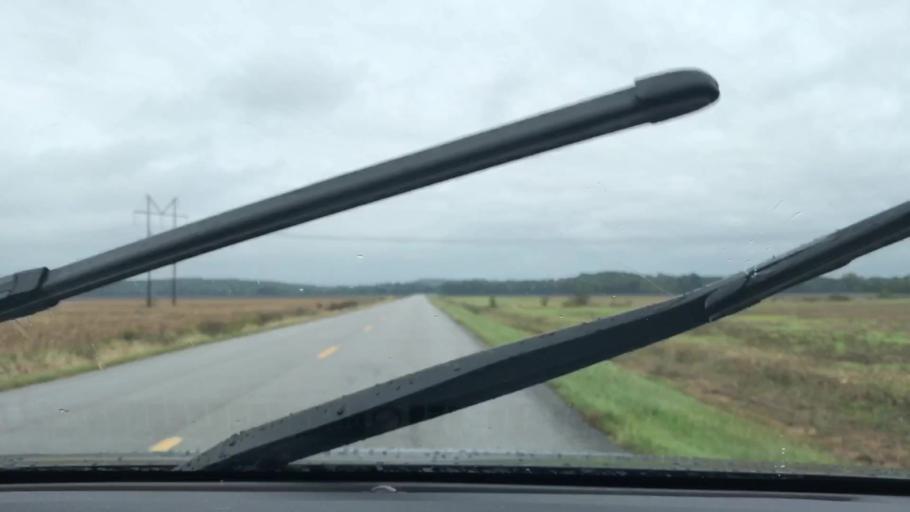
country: US
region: Kentucky
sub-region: McLean County
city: Calhoun
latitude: 37.5048
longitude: -87.2500
